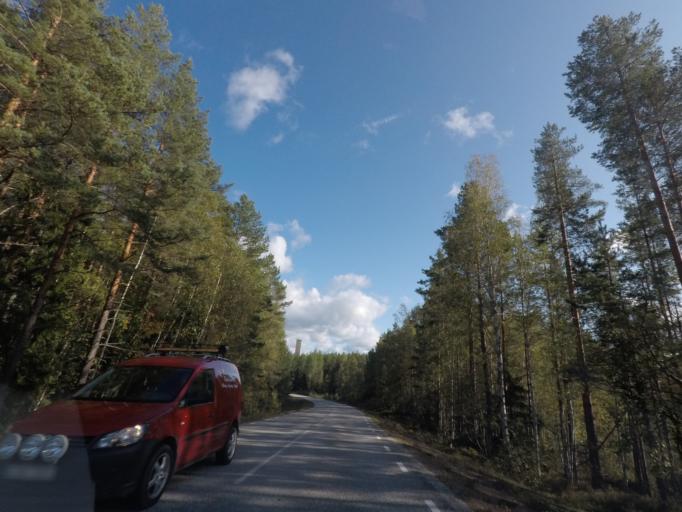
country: SE
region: Vaestmanland
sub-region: Skinnskattebergs Kommun
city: Skinnskatteberg
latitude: 59.8316
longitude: 15.5541
